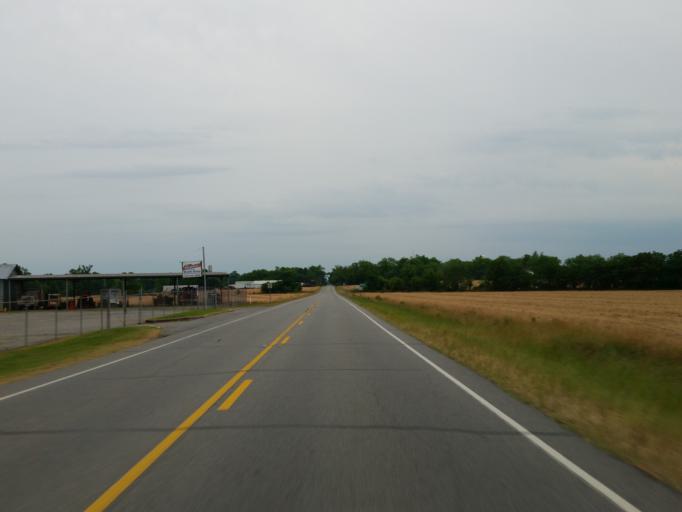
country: US
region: Georgia
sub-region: Dooly County
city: Unadilla
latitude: 32.2042
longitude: -83.7603
